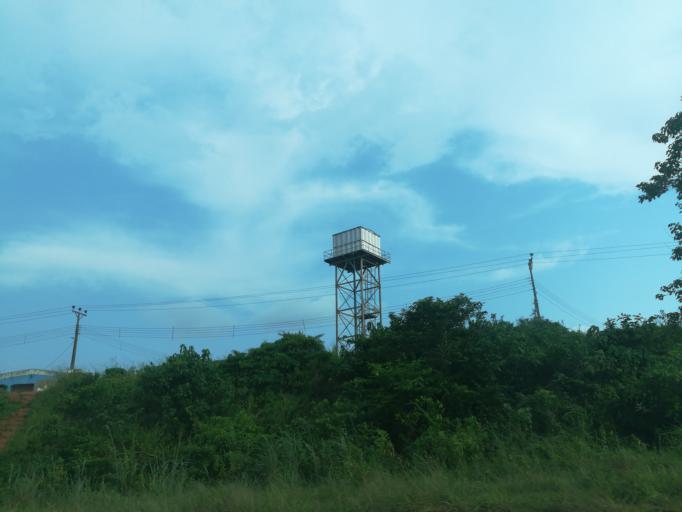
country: NG
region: Lagos
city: Ikorodu
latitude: 6.6231
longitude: 3.6620
